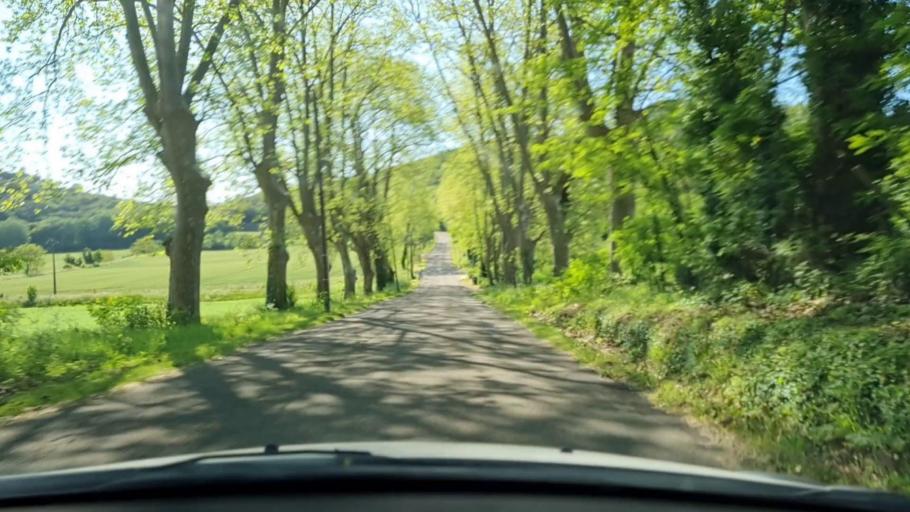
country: FR
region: Languedoc-Roussillon
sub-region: Departement du Gard
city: Cendras
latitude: 44.1510
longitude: 4.0454
